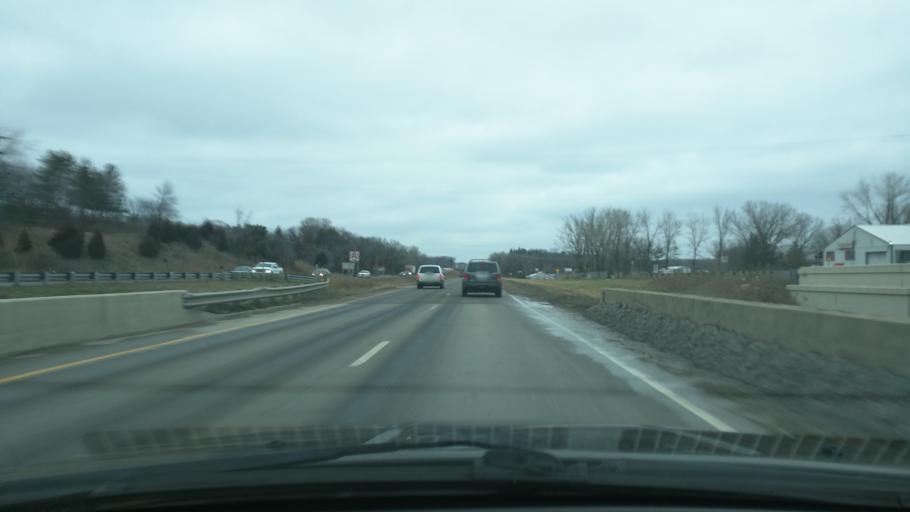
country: US
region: Minnesota
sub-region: Dakota County
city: Inver Grove Heights
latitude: 44.7966
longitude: -93.0379
